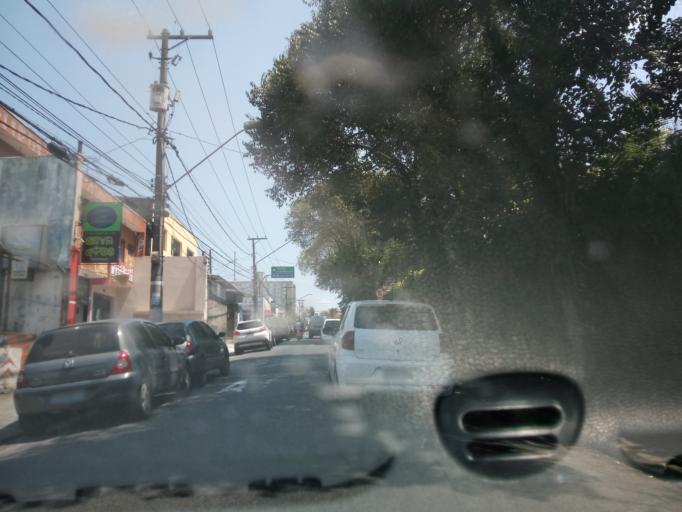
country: BR
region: Sao Paulo
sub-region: Sao Bernardo Do Campo
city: Sao Bernardo do Campo
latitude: -23.7204
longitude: -46.5670
